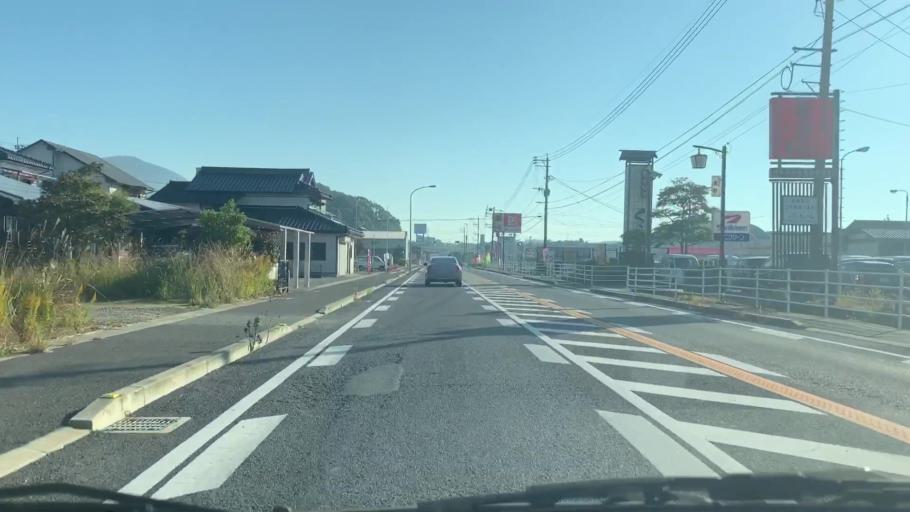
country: JP
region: Saga Prefecture
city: Takeocho-takeo
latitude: 33.2203
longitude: 130.0653
